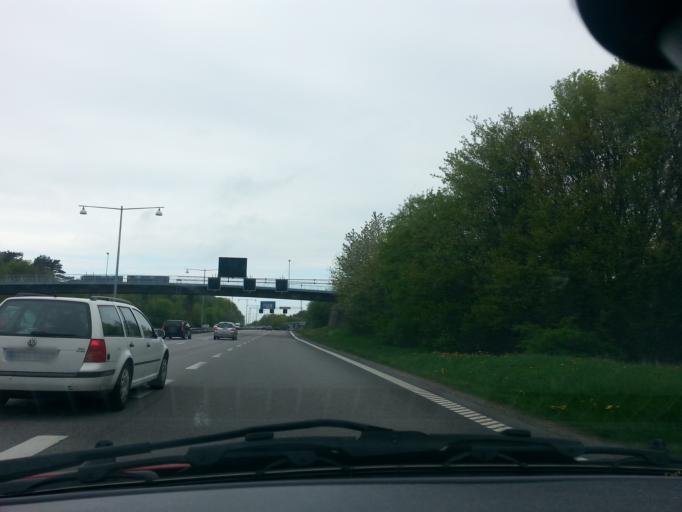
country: SE
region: Vaestra Goetaland
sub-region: Goteborg
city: Majorna
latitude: 57.6632
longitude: 11.8910
